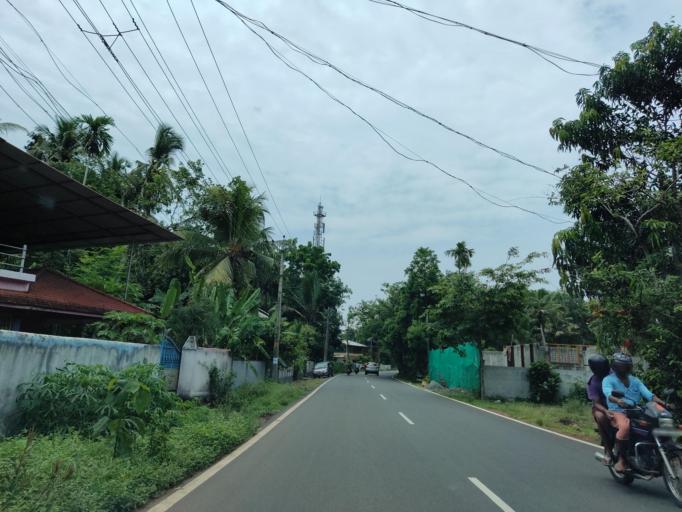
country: IN
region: Kerala
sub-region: Alappuzha
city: Mavelikara
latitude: 9.2670
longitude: 76.5998
